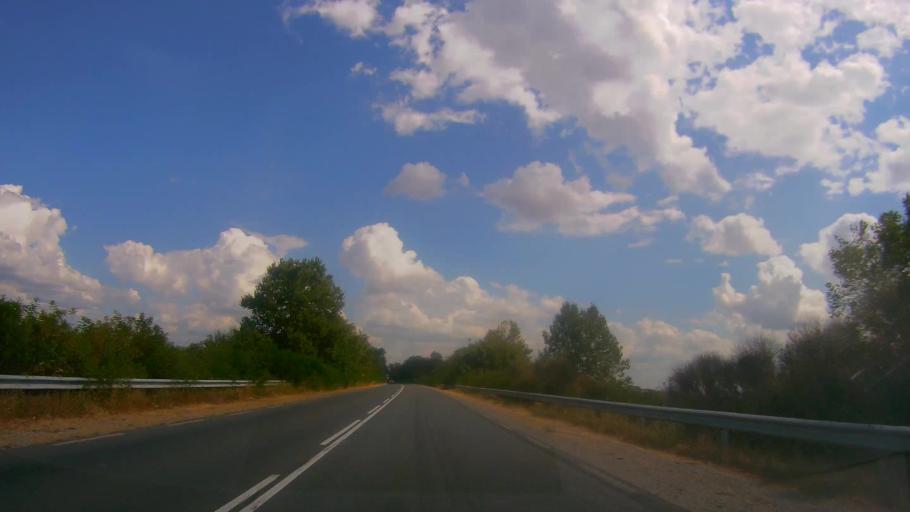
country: BG
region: Sliven
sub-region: Obshtina Sliven
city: Kermen
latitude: 42.6317
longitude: 26.1748
